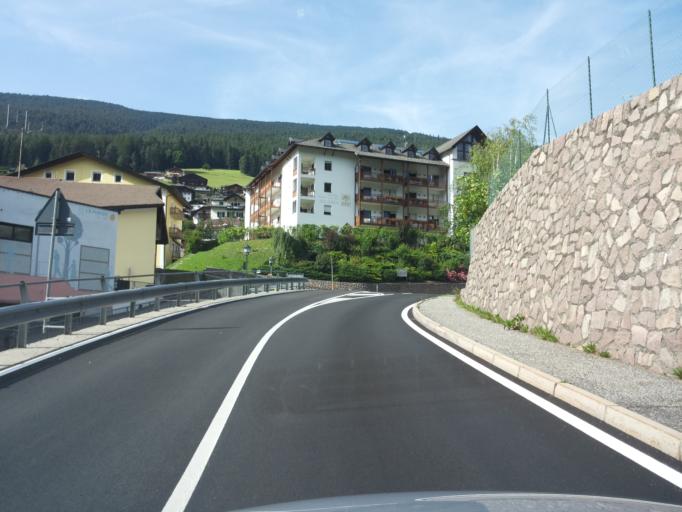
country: IT
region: Trentino-Alto Adige
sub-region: Bolzano
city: Ortisei
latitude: 46.5745
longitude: 11.6678
